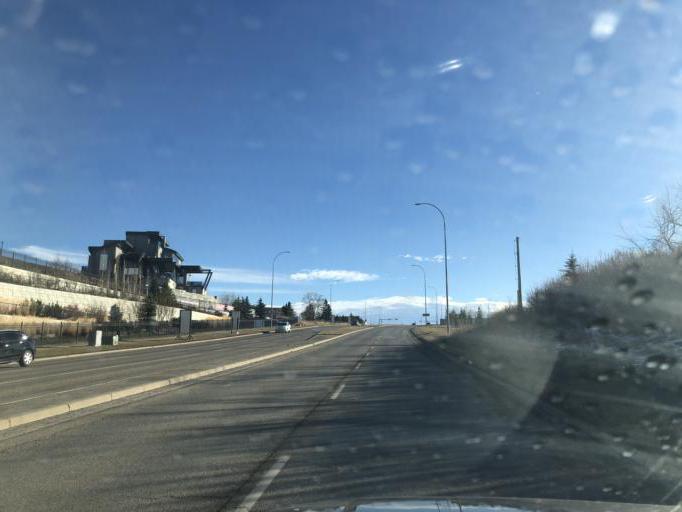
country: CA
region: Alberta
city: Calgary
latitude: 51.0379
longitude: -114.1989
